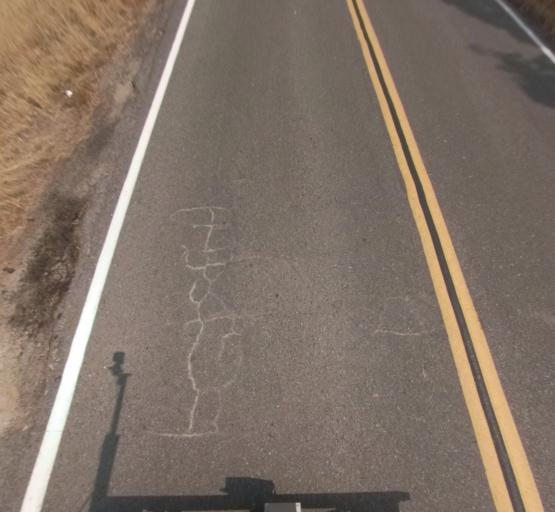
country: US
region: California
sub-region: Madera County
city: Yosemite Lakes
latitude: 37.1732
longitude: -119.9120
